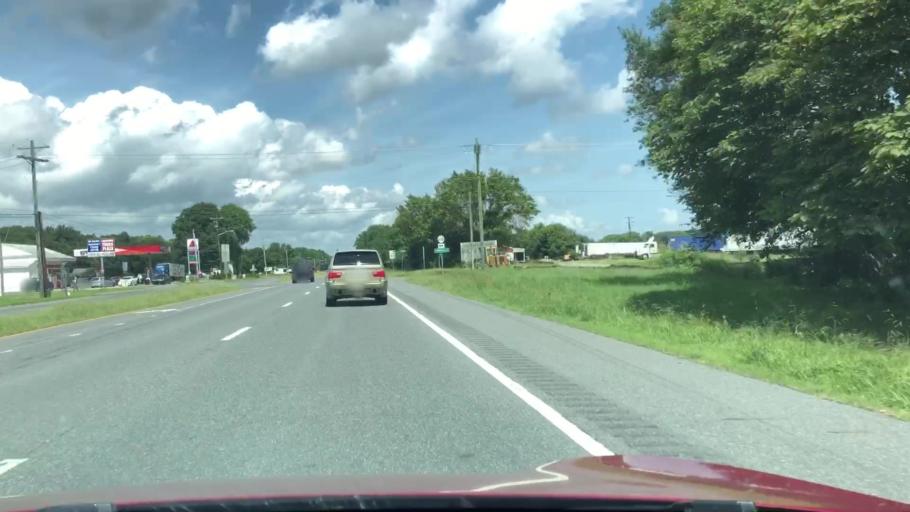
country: US
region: Virginia
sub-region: Northampton County
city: Cape Charles
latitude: 37.1866
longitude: -75.9681
